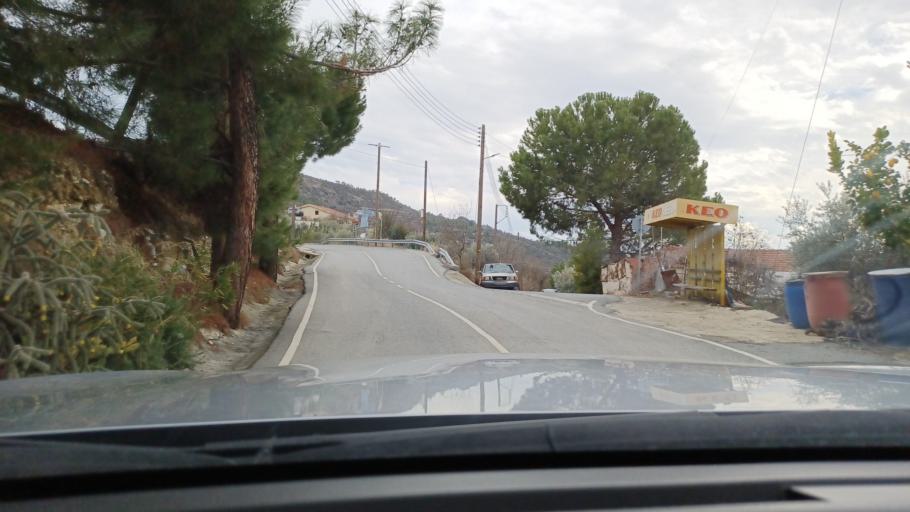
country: CY
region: Limassol
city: Pelendri
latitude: 34.8097
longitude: 32.9116
